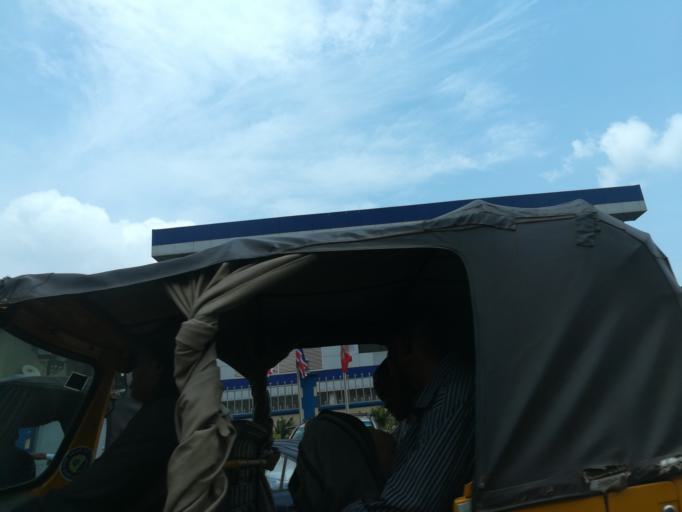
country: NG
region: Lagos
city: Oshodi
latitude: 6.5469
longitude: 3.3307
